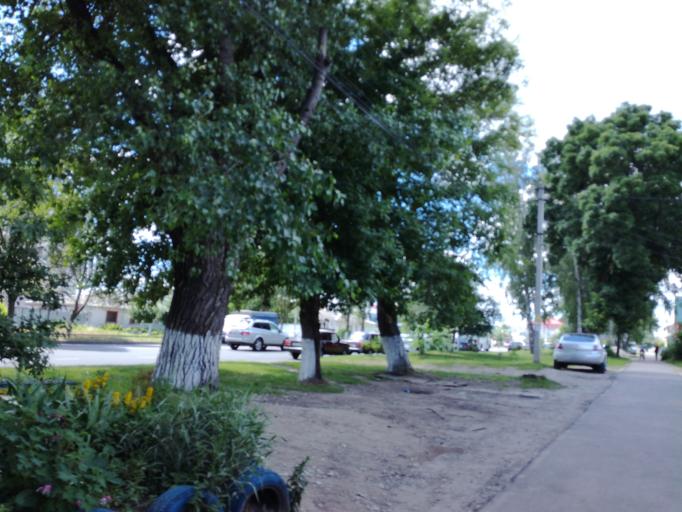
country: RU
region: Kursk
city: Kursk
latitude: 51.7556
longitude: 36.2267
